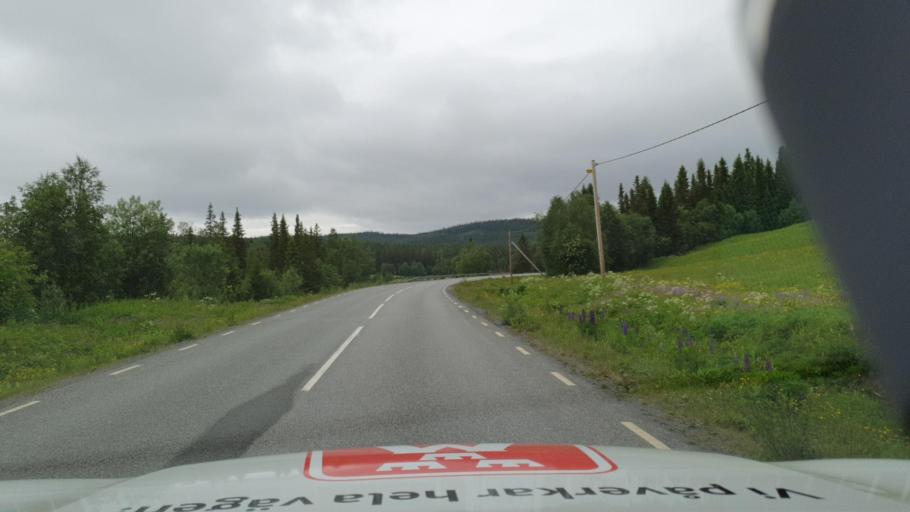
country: SE
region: Jaemtland
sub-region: Are Kommun
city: Are
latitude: 63.6679
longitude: 13.0474
